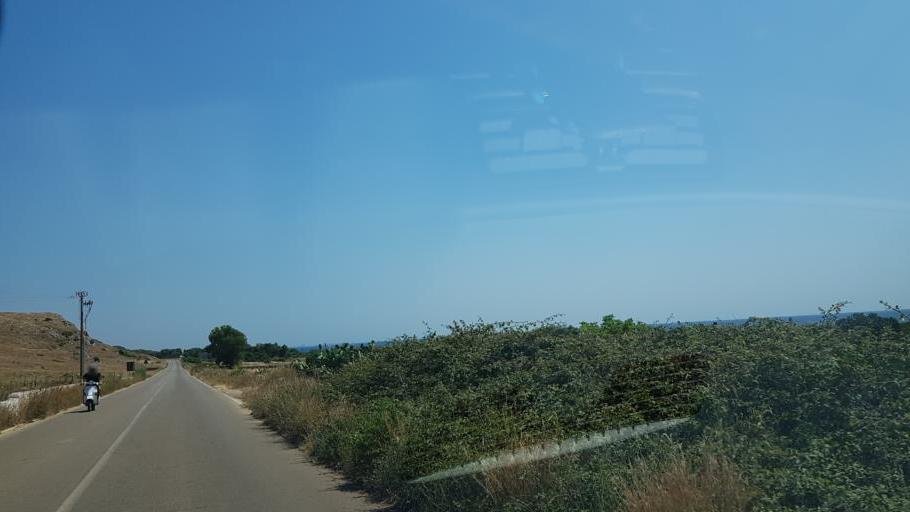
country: IT
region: Apulia
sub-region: Provincia di Lecce
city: Nardo
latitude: 40.1751
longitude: 17.9456
